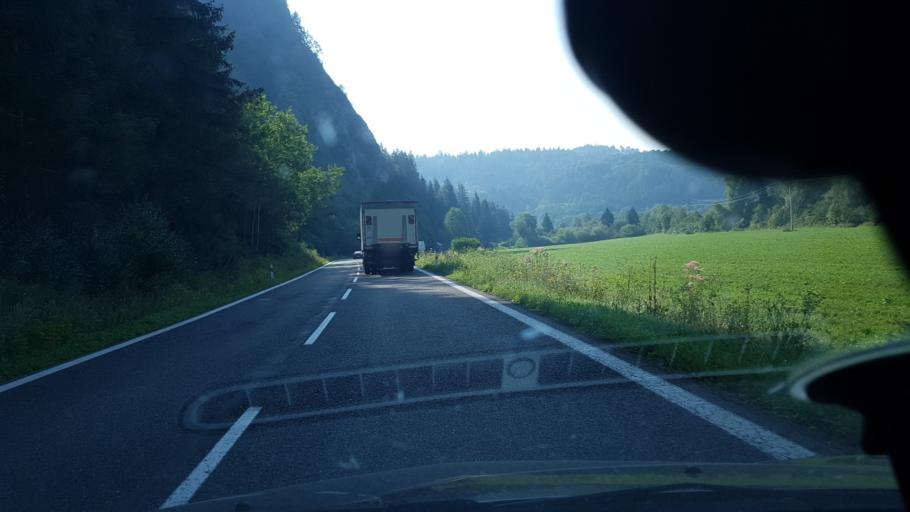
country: SK
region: Zilinsky
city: Tvrdosin
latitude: 49.2973
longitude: 19.4872
